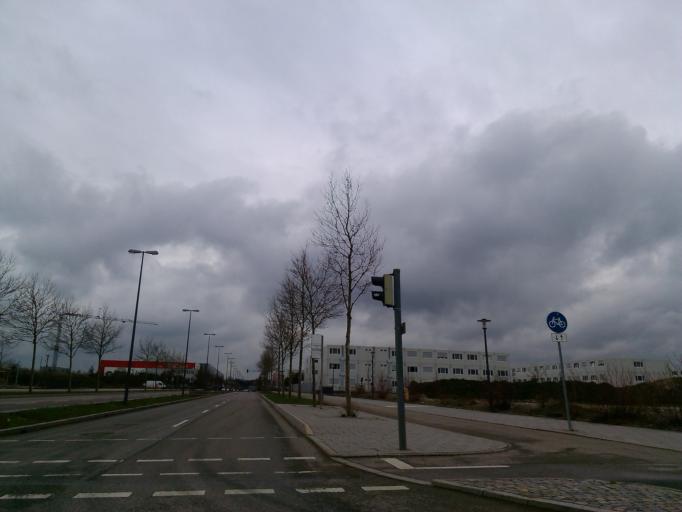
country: DE
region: Bavaria
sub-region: Upper Bavaria
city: Grafelfing
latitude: 48.1382
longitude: 11.4090
